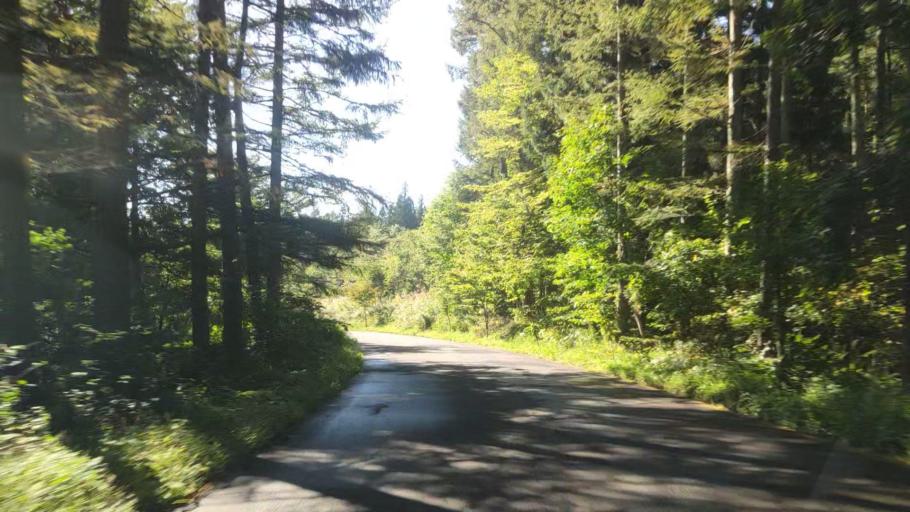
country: JP
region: Nagano
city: Iiyama
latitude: 36.8085
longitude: 138.4249
